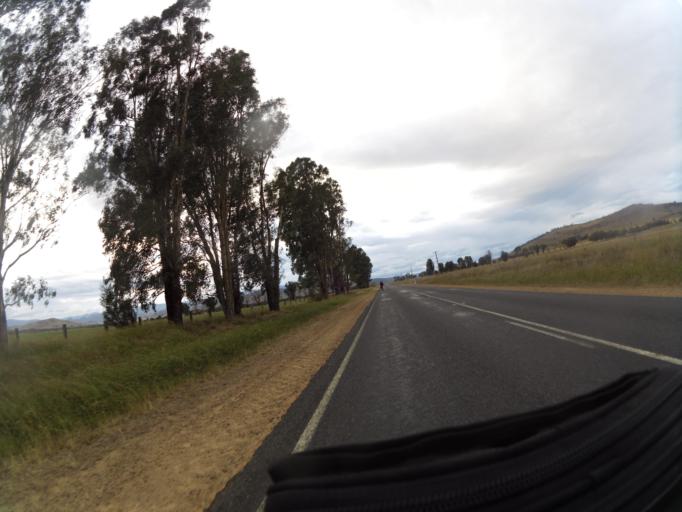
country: AU
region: New South Wales
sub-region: Greater Hume Shire
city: Holbrook
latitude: -36.0679
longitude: 147.9563
